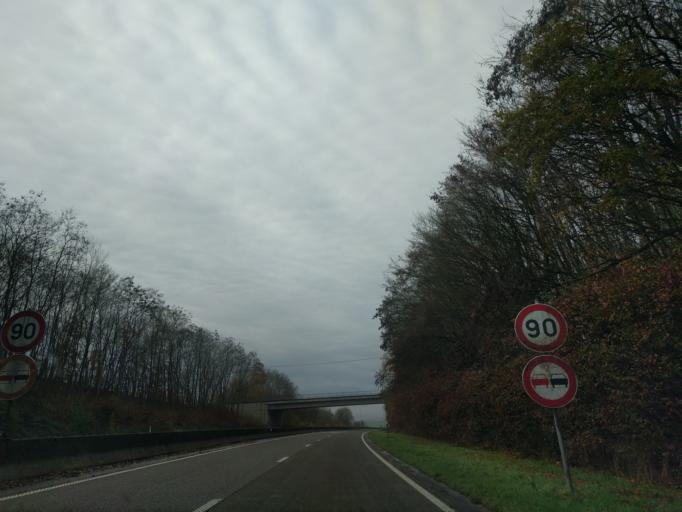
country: BE
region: Wallonia
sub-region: Province de Namur
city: Onhaye
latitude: 50.2433
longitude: 4.8301
